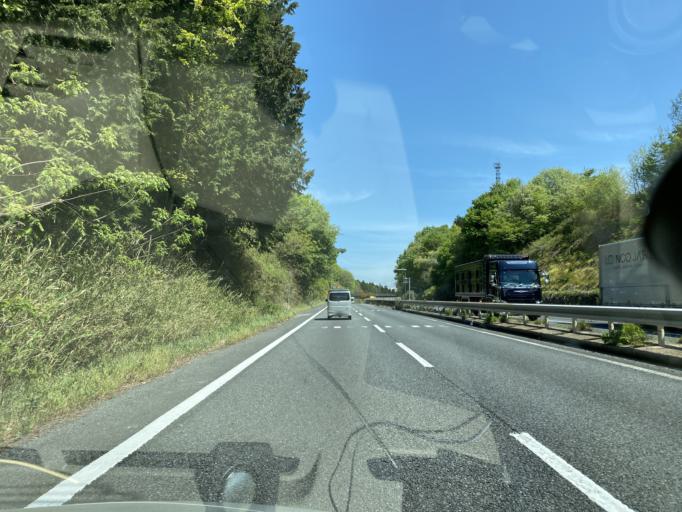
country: JP
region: Mie
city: Nabari
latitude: 34.6669
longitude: 136.0328
